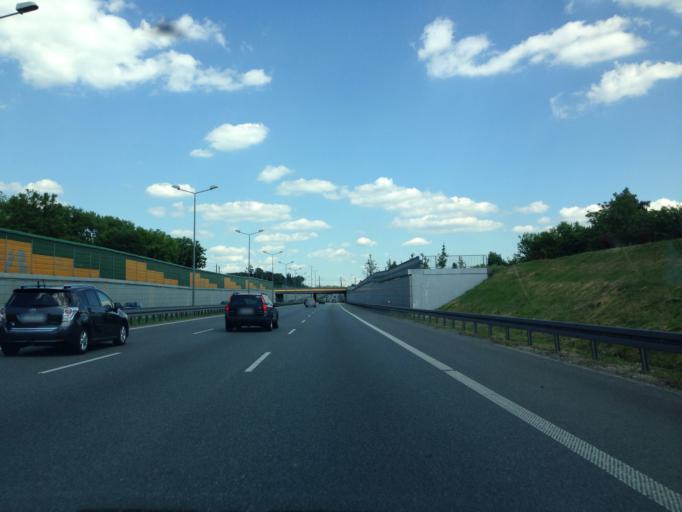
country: PL
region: Masovian Voivodeship
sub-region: Warszawa
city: Bemowo
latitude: 52.2467
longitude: 20.9182
